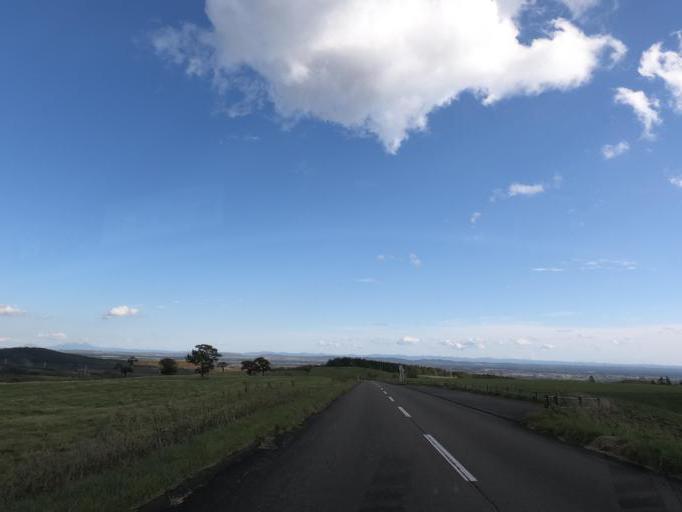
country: JP
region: Hokkaido
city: Otofuke
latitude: 43.2781
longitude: 143.2273
